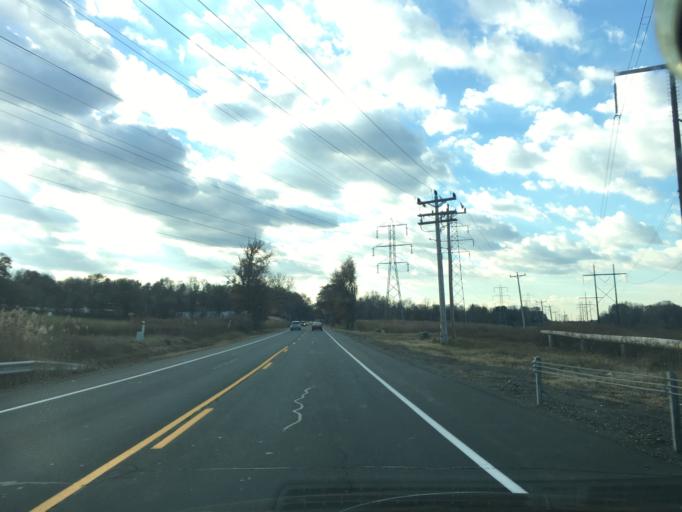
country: US
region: New York
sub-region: Albany County
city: Menands
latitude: 42.6692
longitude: -73.6913
